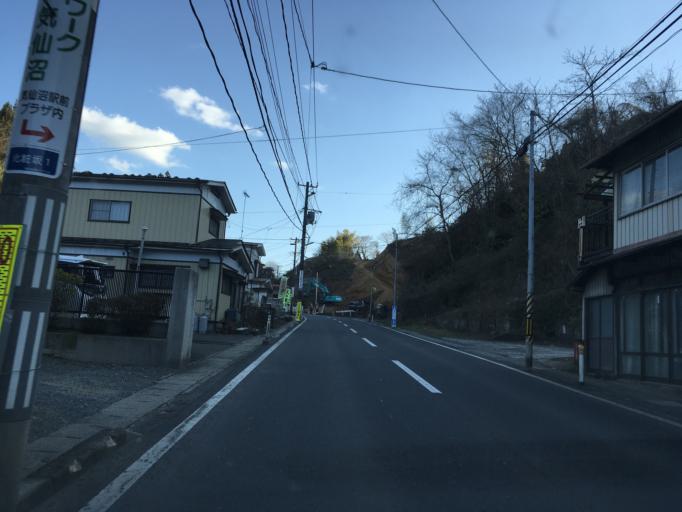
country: JP
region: Iwate
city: Ofunato
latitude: 38.9049
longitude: 141.5644
